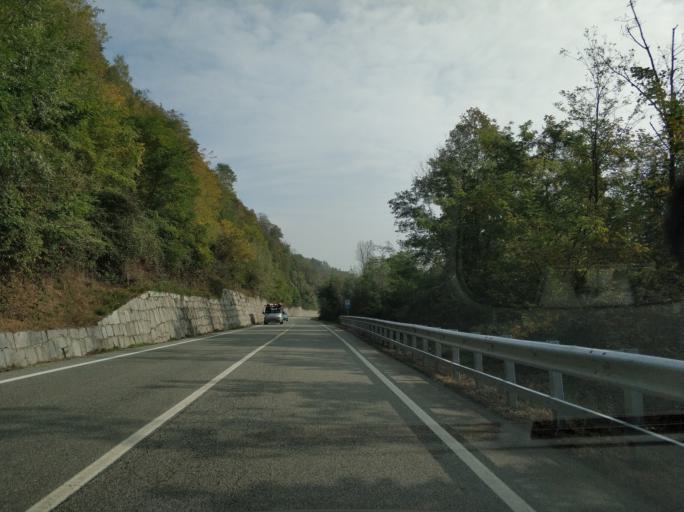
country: IT
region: Piedmont
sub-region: Provincia di Biella
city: Netro
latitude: 45.5219
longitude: 7.9383
